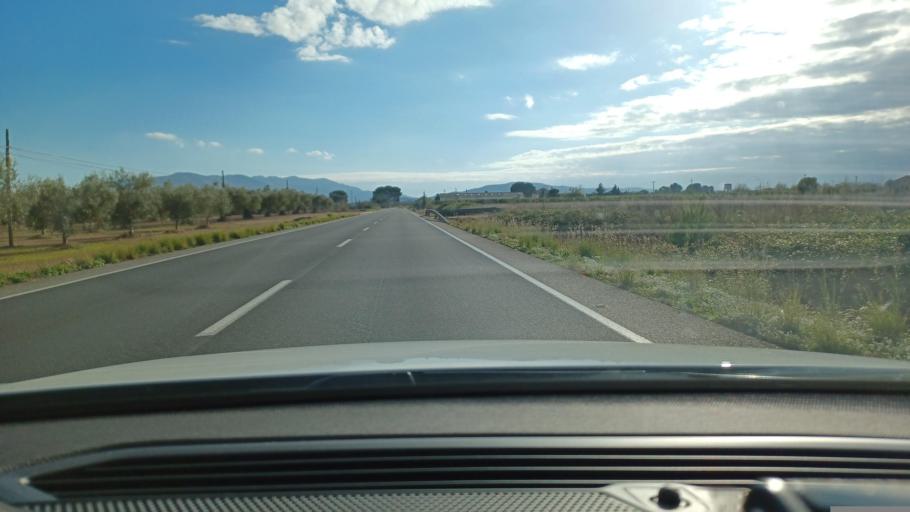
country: ES
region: Catalonia
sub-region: Provincia de Tarragona
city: Santa Barbara
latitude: 40.7311
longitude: 0.5032
